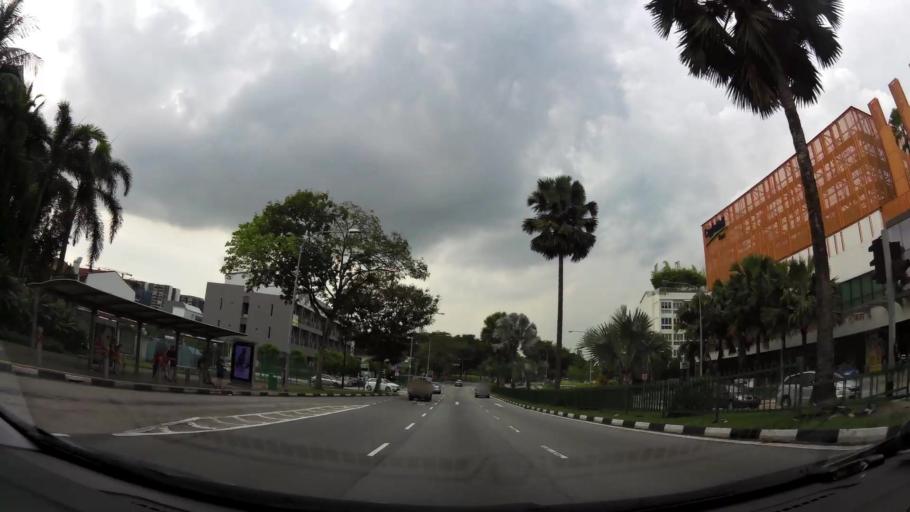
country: MY
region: Johor
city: Kampung Pasir Gudang Baru
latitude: 1.4414
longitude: 103.8243
